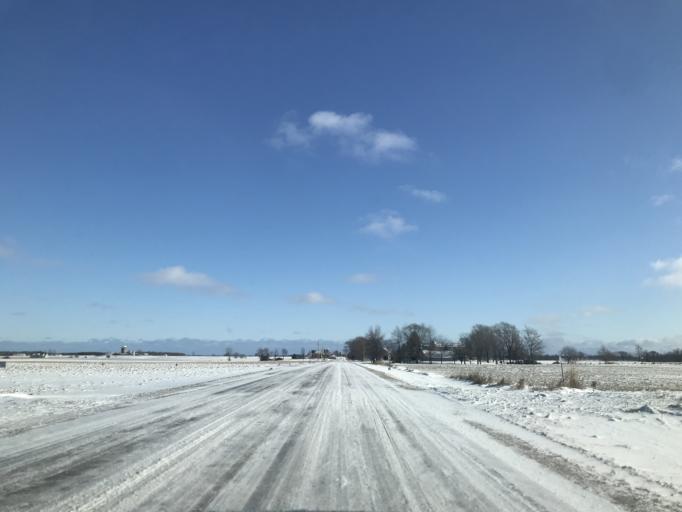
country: US
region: Wisconsin
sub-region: Kewaunee County
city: Luxemburg
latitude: 44.6978
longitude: -87.6180
